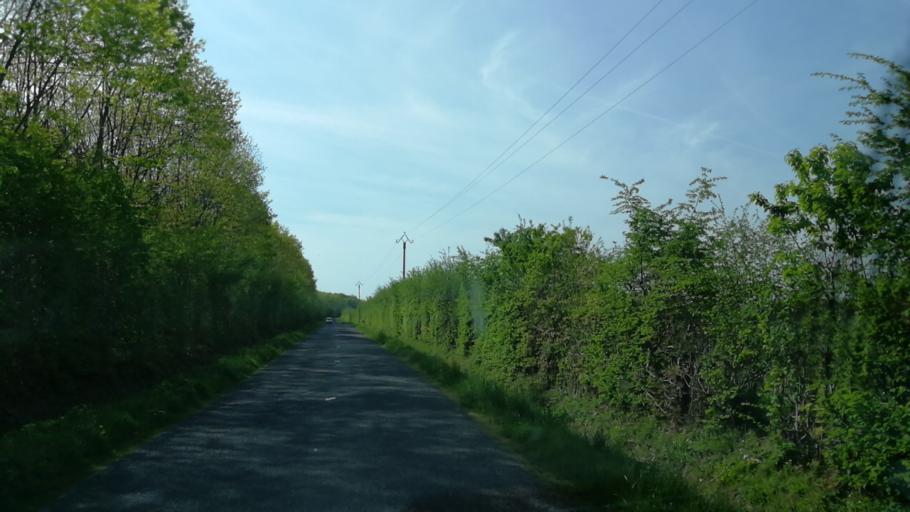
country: FR
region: Auvergne
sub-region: Departement de l'Allier
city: Neuilly-le-Real
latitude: 46.4995
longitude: 3.5024
